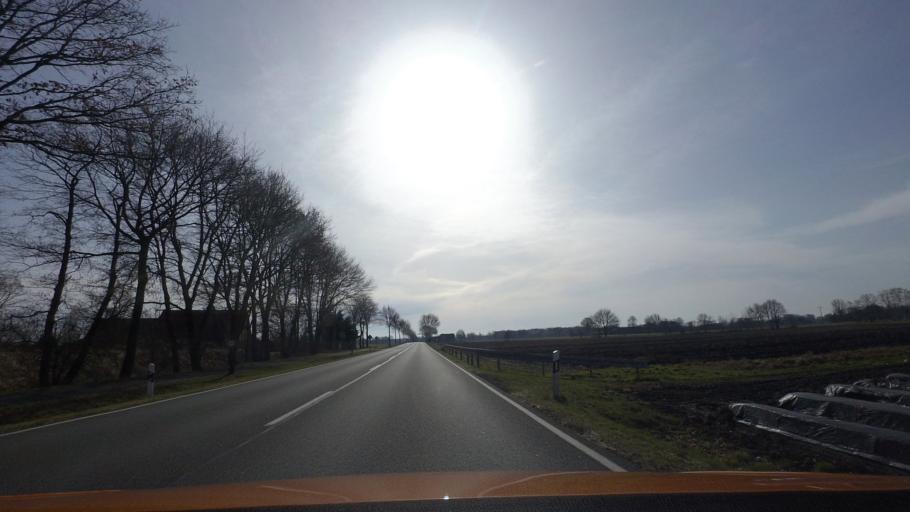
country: DE
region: Lower Saxony
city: Uchte
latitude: 52.4640
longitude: 8.9115
